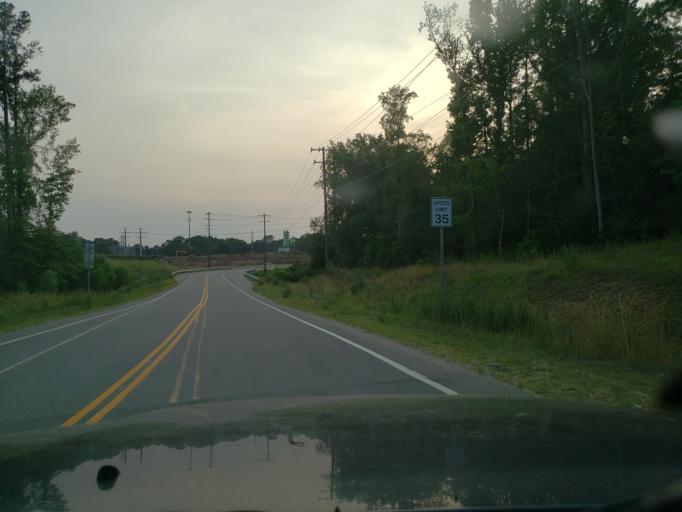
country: US
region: North Carolina
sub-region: Durham County
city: Durham
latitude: 35.9821
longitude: -78.8556
